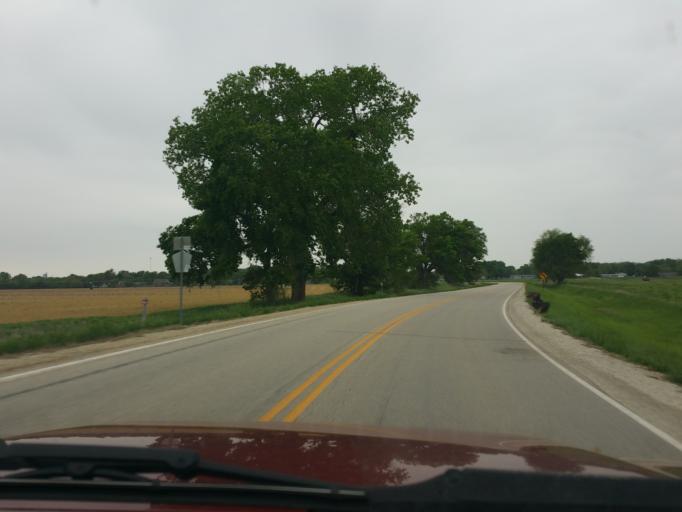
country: US
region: Kansas
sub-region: Riley County
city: Manhattan
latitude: 39.2345
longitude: -96.5724
